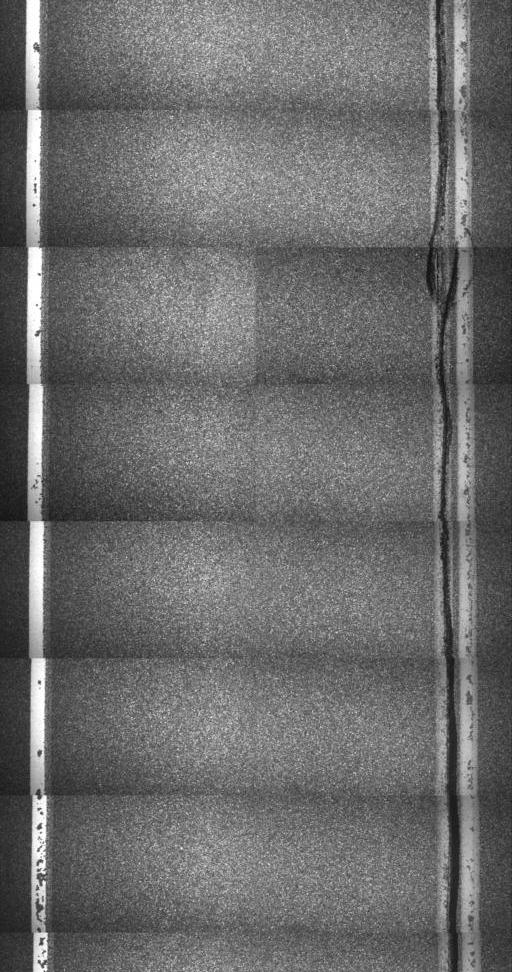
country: US
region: Vermont
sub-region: Lamoille County
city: Morrisville
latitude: 44.4735
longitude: -72.5308
